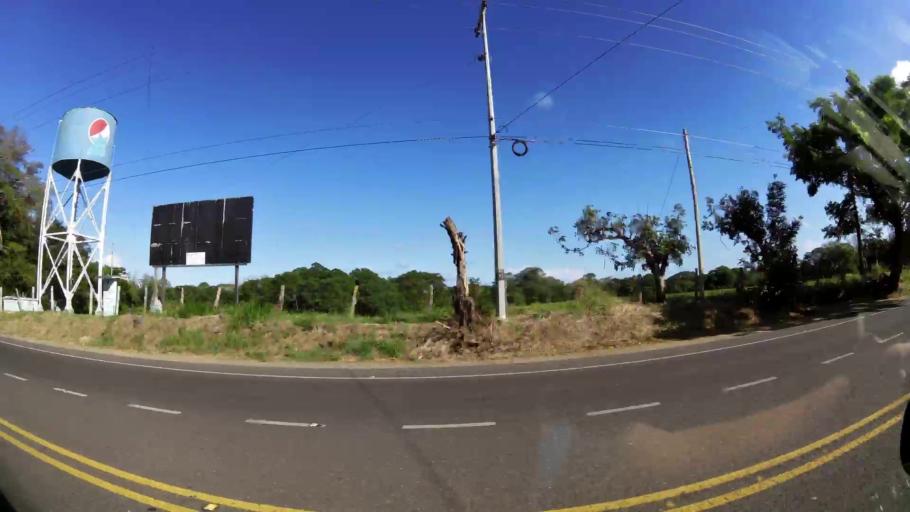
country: CR
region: Guanacaste
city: Sardinal
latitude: 10.5583
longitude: -85.5915
